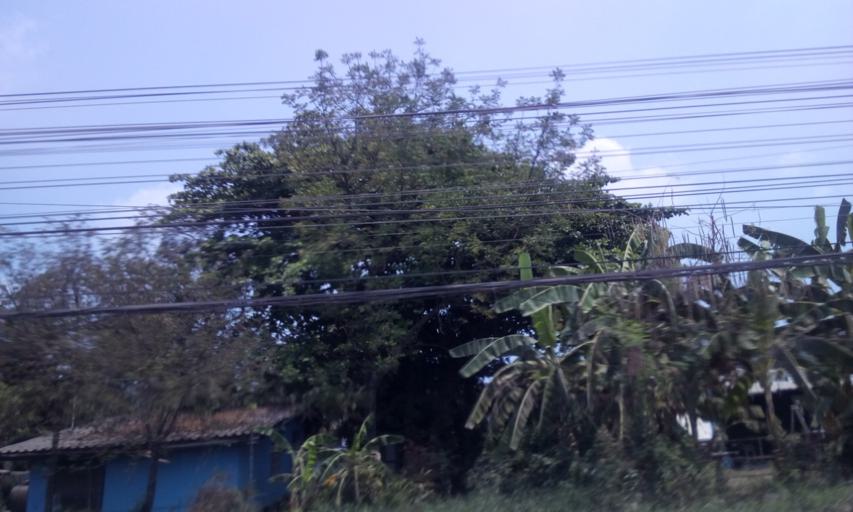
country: TH
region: Chachoengsao
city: Chachoengsao
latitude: 13.6495
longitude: 101.0989
